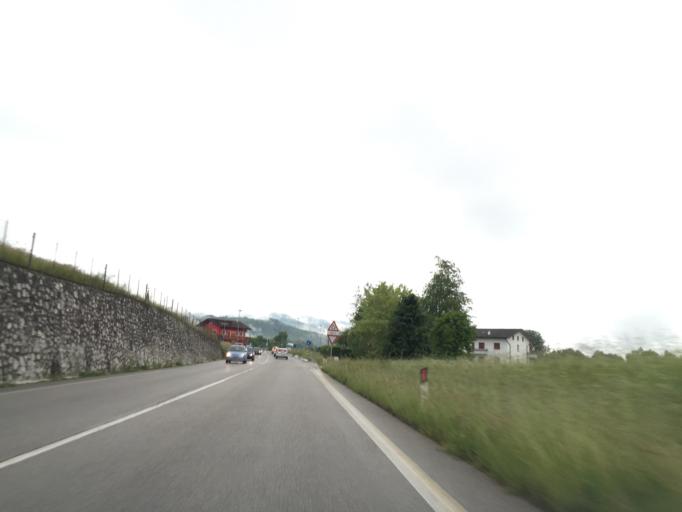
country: IT
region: Veneto
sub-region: Provincia di Belluno
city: Limana
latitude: 46.0984
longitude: 12.1735
